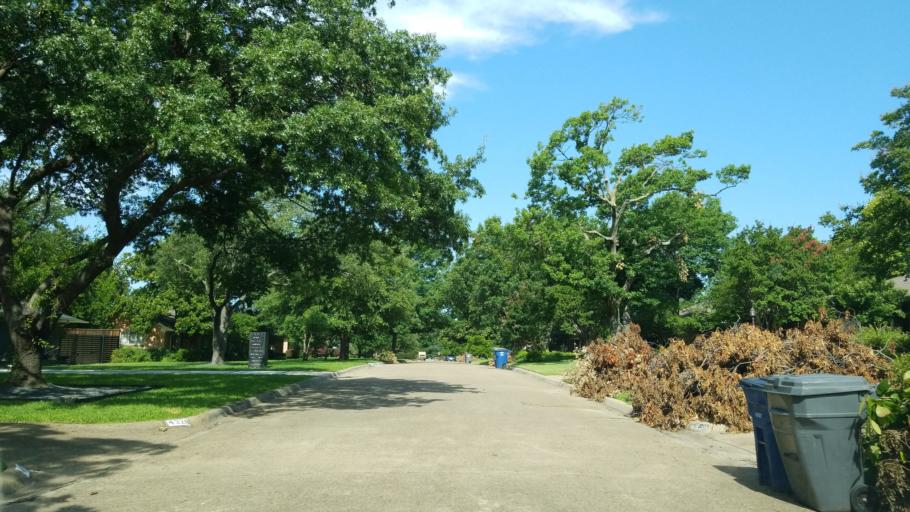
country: US
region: Texas
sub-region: Dallas County
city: Addison
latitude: 32.9089
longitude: -96.8351
